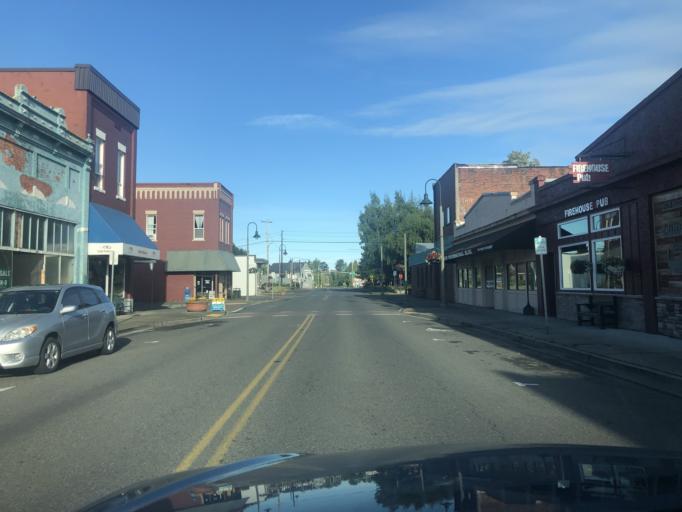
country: US
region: Washington
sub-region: Pierce County
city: Buckley
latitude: 47.1630
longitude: -122.0278
